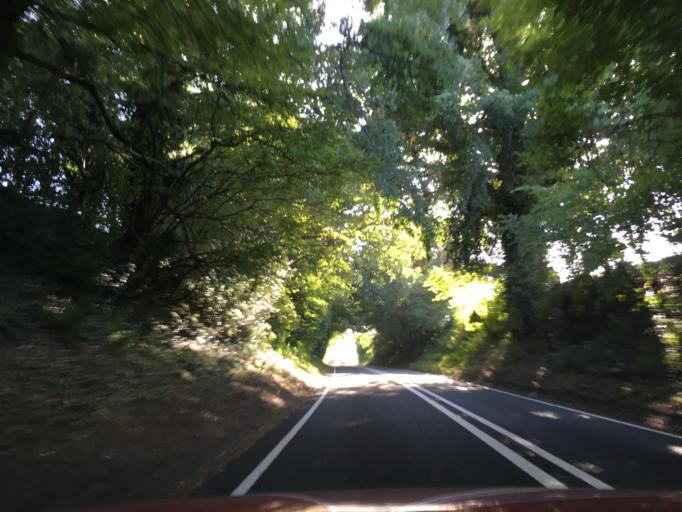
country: GB
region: England
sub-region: Hampshire
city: Four Marks
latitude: 51.0216
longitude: -1.0791
